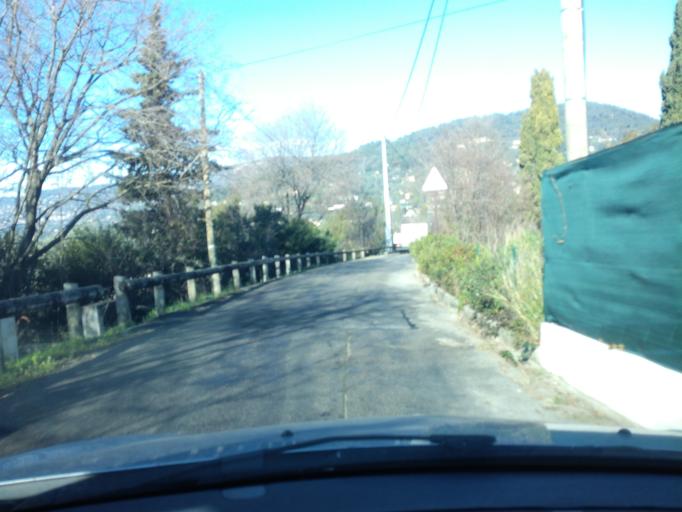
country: FR
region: Provence-Alpes-Cote d'Azur
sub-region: Departement des Alpes-Maritimes
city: Grasse
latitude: 43.6438
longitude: 6.9061
